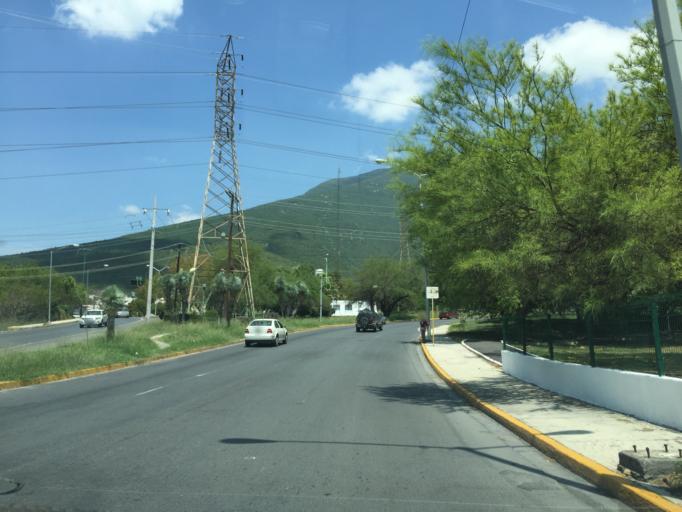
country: MX
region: Nuevo Leon
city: Guadalupe
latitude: 25.6476
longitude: -100.2696
